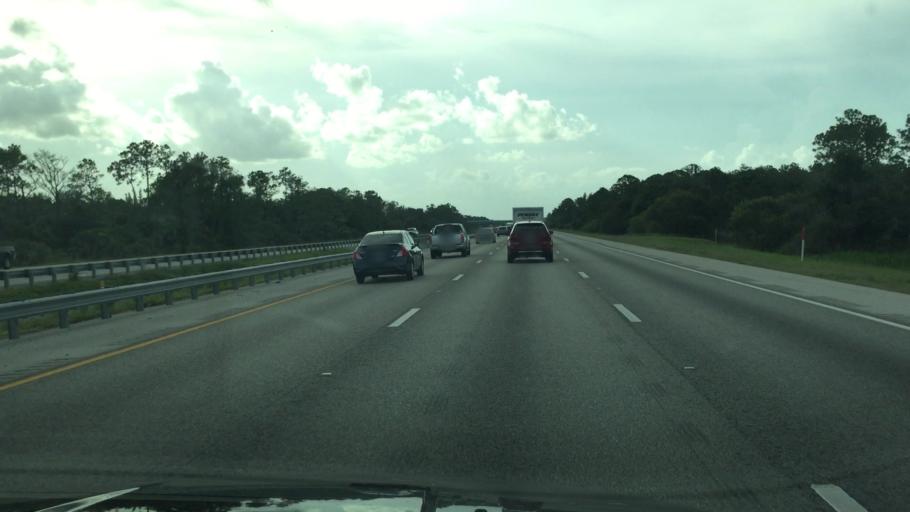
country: US
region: Florida
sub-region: Lee County
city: Suncoast Estates
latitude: 26.7339
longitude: -81.8428
